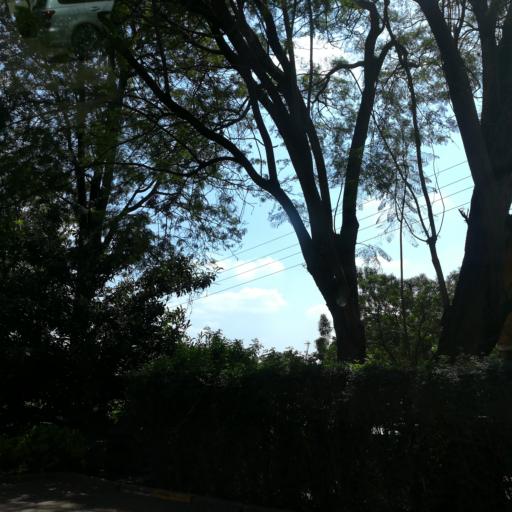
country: KE
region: Nairobi Area
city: Nairobi
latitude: -1.2977
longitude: 36.7987
